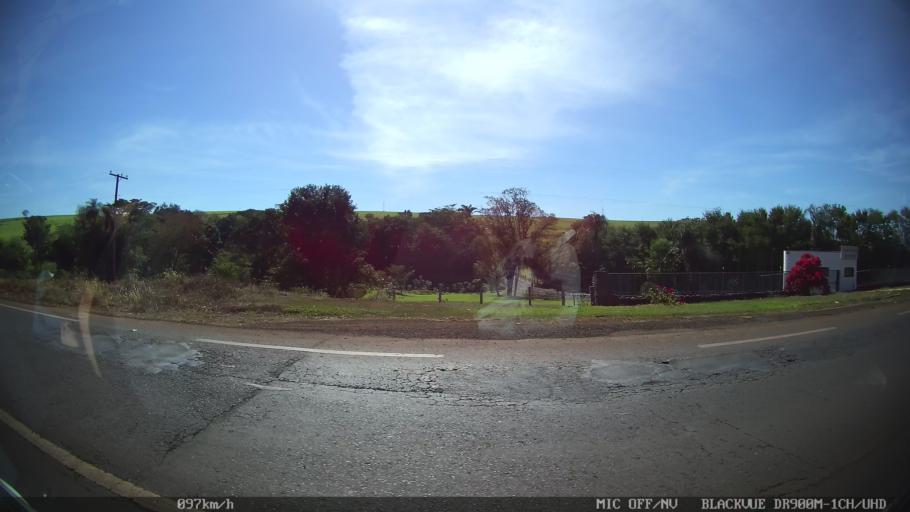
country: BR
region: Sao Paulo
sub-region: Ipua
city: Ipua
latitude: -20.4928
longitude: -48.0152
